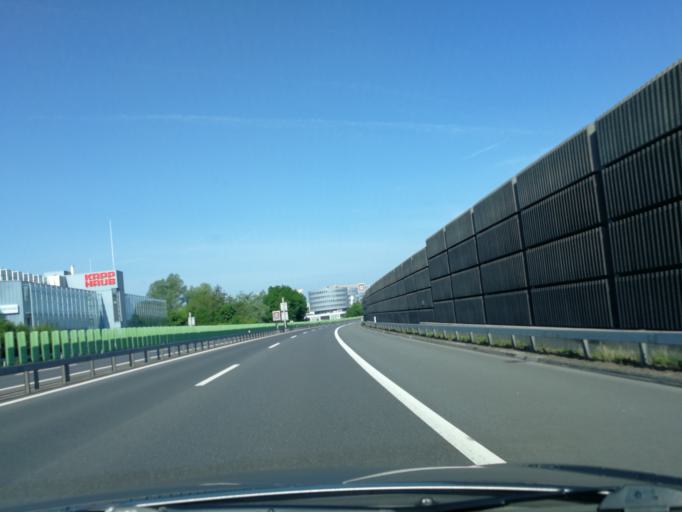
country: CH
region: Zug
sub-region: Zug
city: Steinhausen
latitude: 47.1879
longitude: 8.4871
